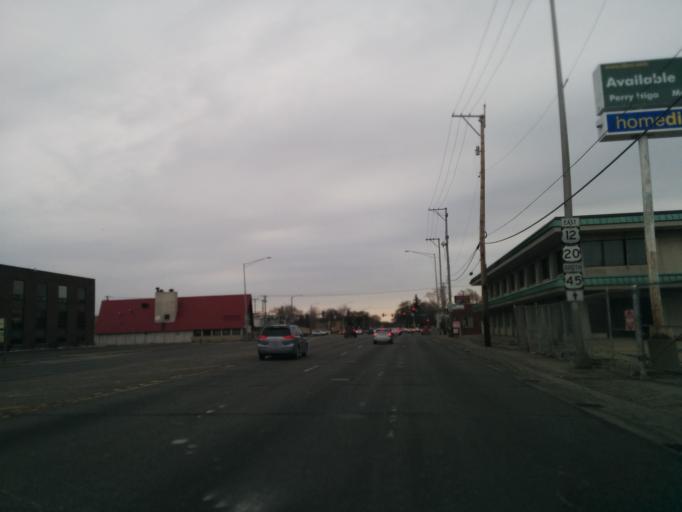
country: US
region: Illinois
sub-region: Cook County
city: Westchester
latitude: 41.8651
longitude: -87.8827
